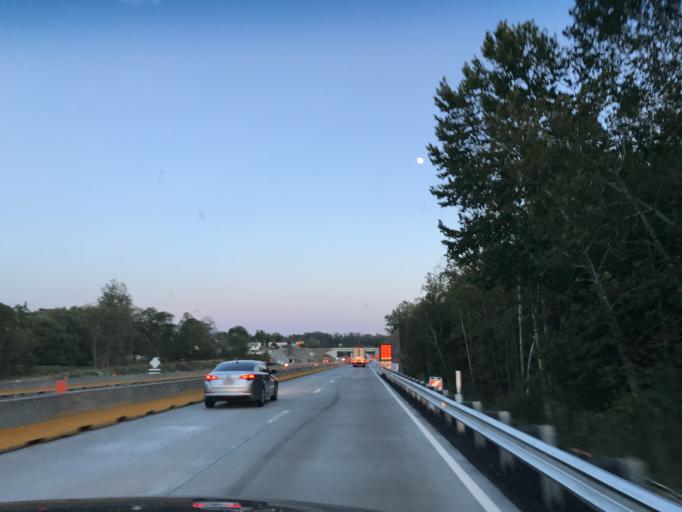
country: US
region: Pennsylvania
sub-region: Washington County
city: Bentleyville
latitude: 40.1362
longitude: -80.0113
